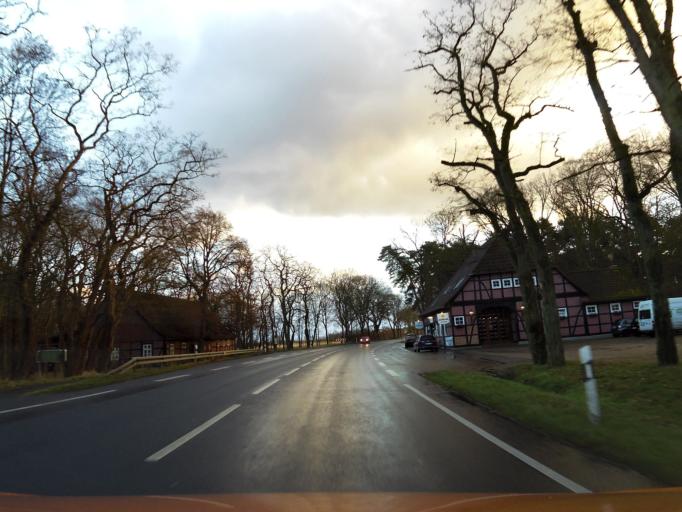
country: DE
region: Lower Saxony
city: Didderse
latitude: 52.3964
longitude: 10.3707
